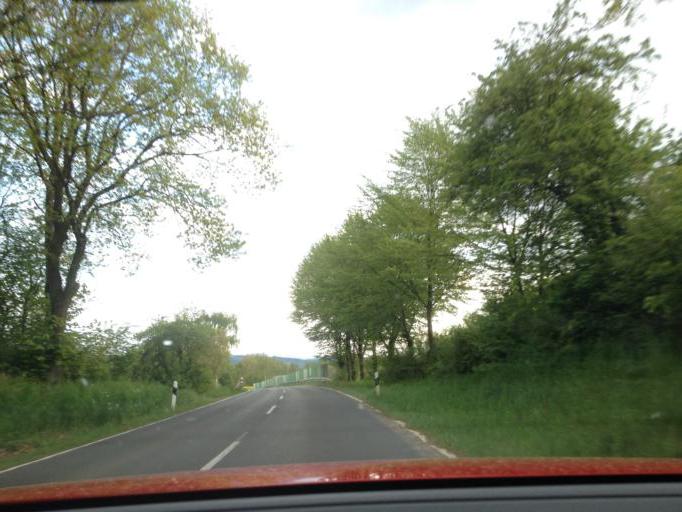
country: DE
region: Bavaria
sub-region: Upper Franconia
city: Arzberg
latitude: 50.0508
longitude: 12.1701
